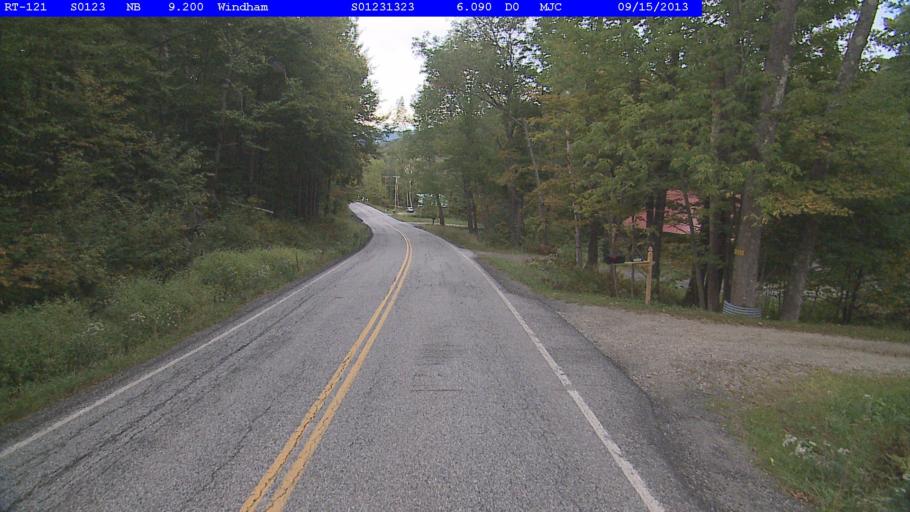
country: US
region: Vermont
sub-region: Windsor County
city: Chester
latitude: 43.2039
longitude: -72.7326
